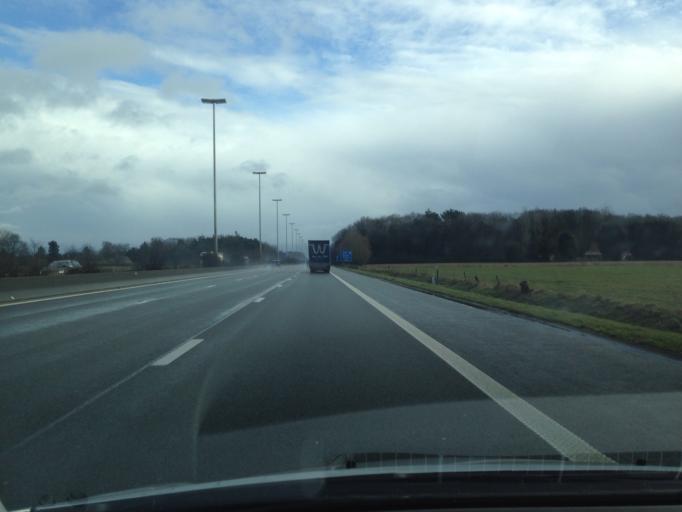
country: BE
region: Flanders
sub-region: Provincie West-Vlaanderen
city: Beernem
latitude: 51.1253
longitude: 3.3089
